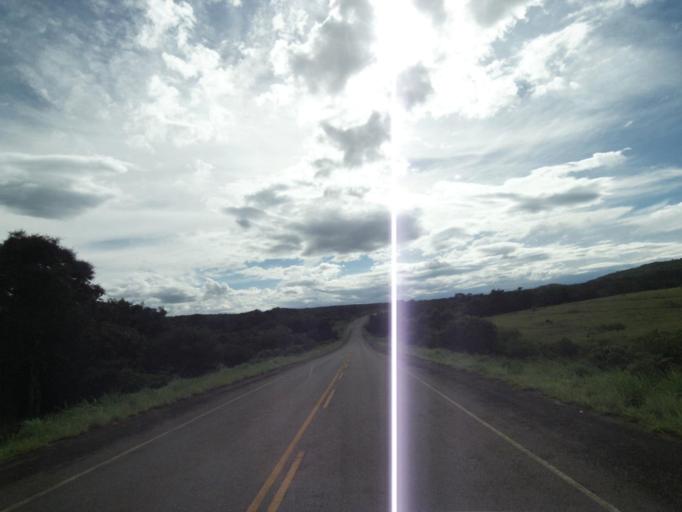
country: BR
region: Goias
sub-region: Jaragua
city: Jaragua
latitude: -15.8389
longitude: -49.2848
